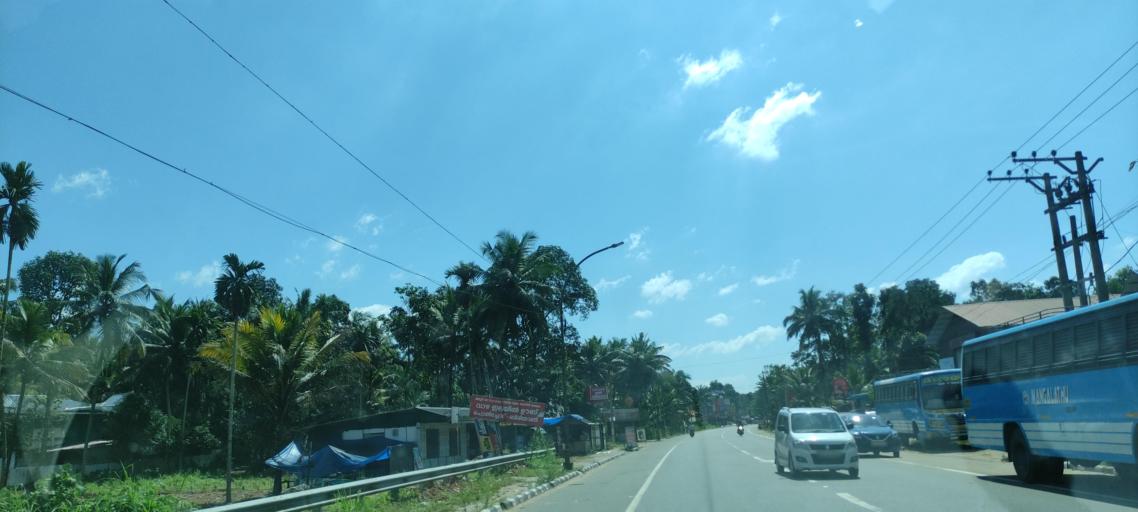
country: IN
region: Kerala
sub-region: Pattanamtitta
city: Adur
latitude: 9.1512
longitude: 76.7284
